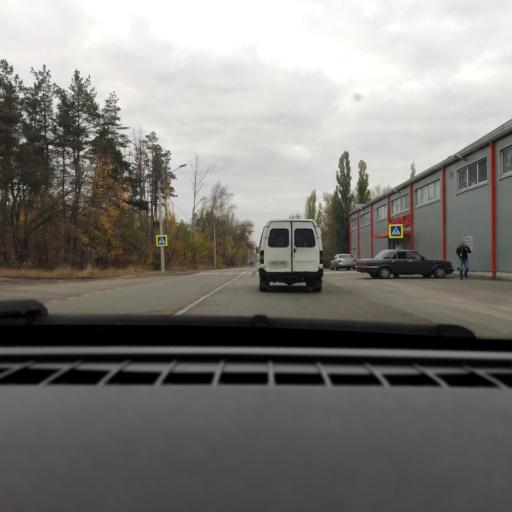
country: RU
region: Voronezj
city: Somovo
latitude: 51.7197
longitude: 39.2947
